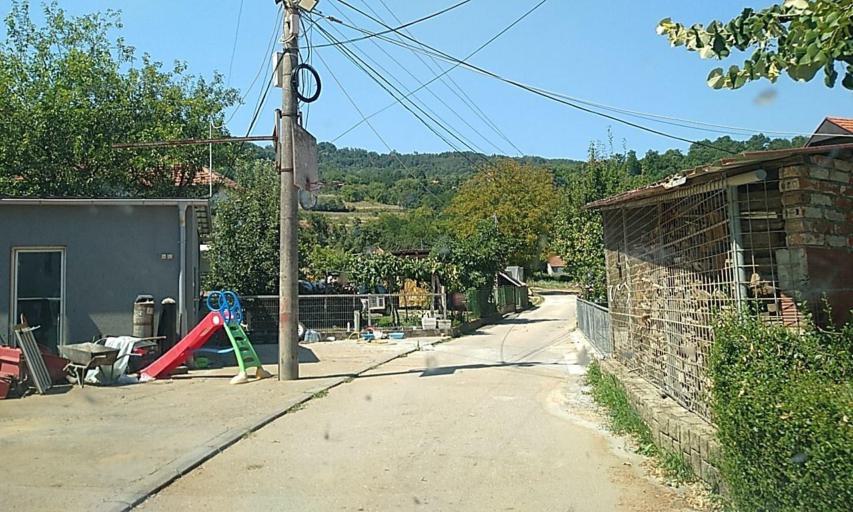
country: RS
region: Central Serbia
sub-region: Pcinjski Okrug
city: Vladicin Han
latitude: 42.7552
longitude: 22.0745
